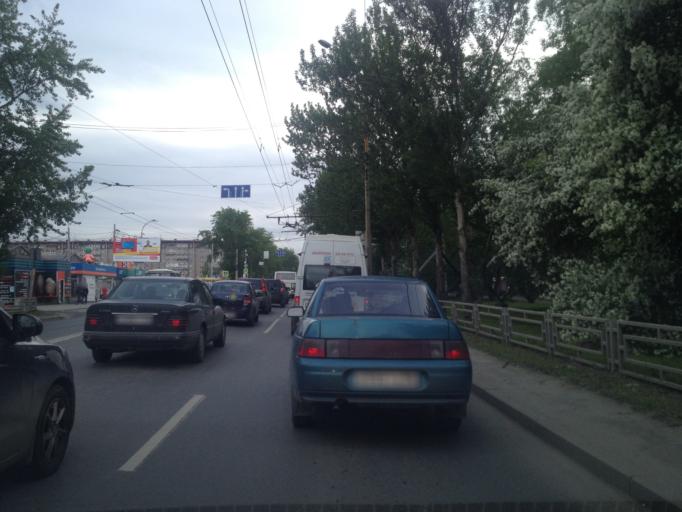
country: RU
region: Sverdlovsk
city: Sovkhoznyy
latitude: 56.7983
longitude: 60.5812
